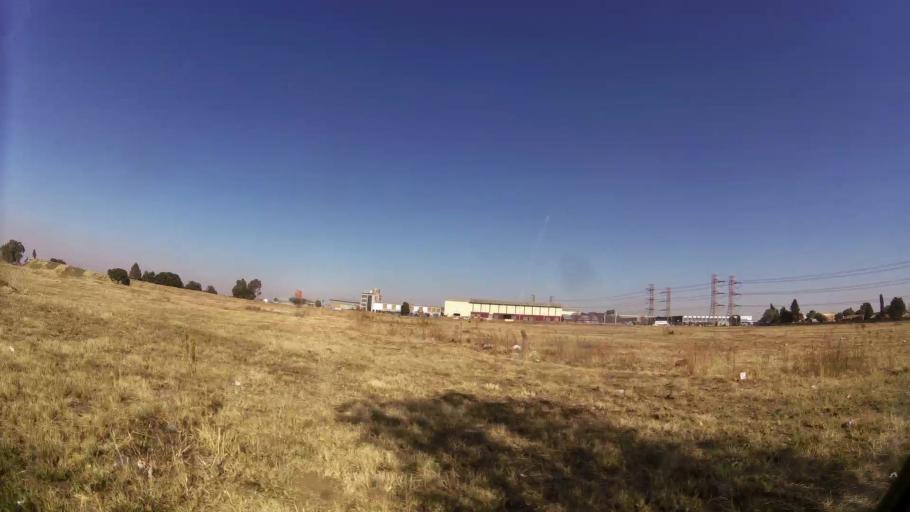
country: ZA
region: Gauteng
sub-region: Ekurhuleni Metropolitan Municipality
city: Germiston
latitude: -26.2439
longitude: 28.1062
